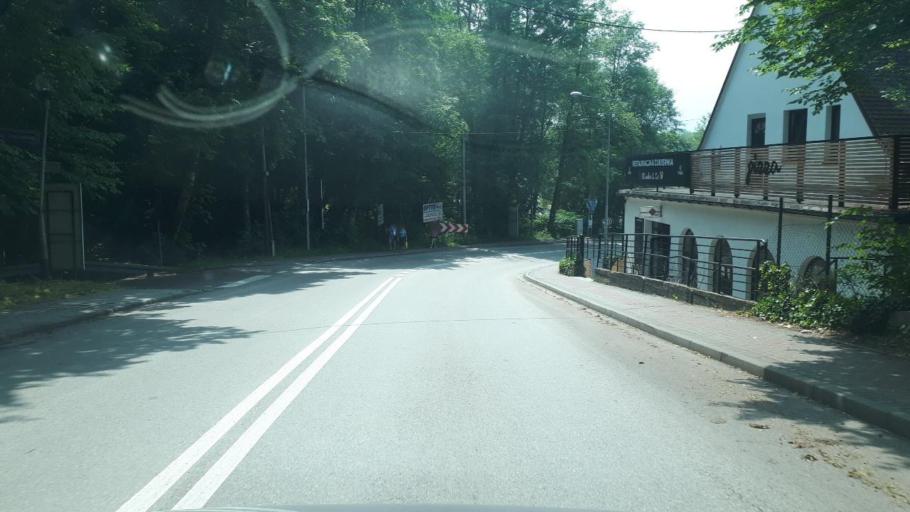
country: PL
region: Silesian Voivodeship
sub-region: Powiat cieszynski
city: Ustron
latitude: 49.7226
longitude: 18.8188
